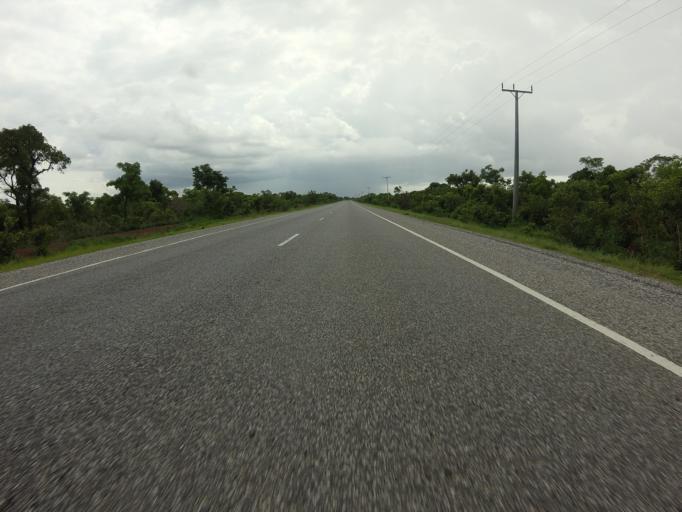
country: GH
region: Northern
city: Tamale
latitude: 9.1341
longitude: -1.3281
